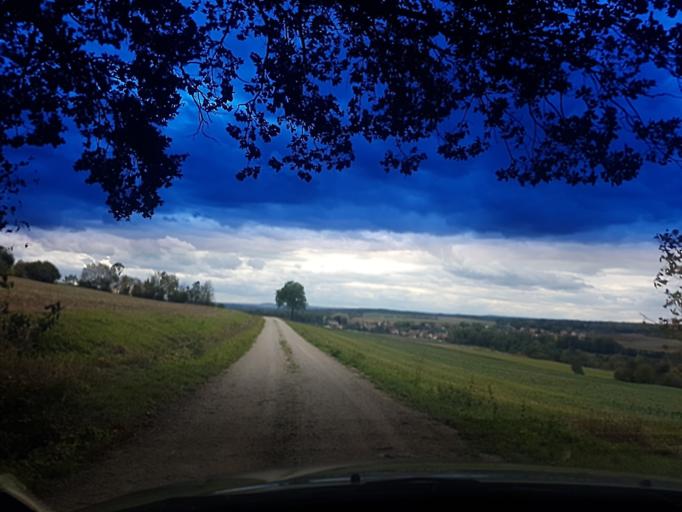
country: DE
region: Bavaria
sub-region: Upper Franconia
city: Schesslitz
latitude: 49.9955
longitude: 11.0620
